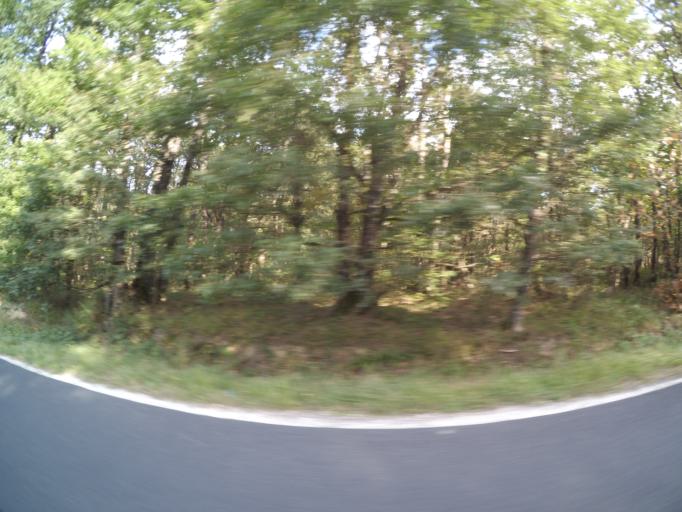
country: FR
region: Centre
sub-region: Departement d'Indre-et-Loire
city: Nazelles-Negron
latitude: 47.4659
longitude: 0.9555
